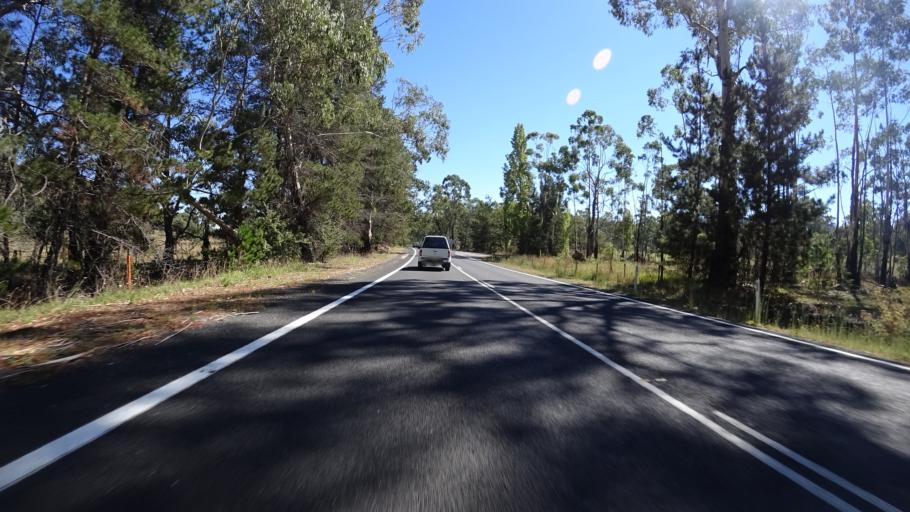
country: AU
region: New South Wales
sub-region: Lithgow
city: Portland
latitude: -33.3155
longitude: 150.0366
